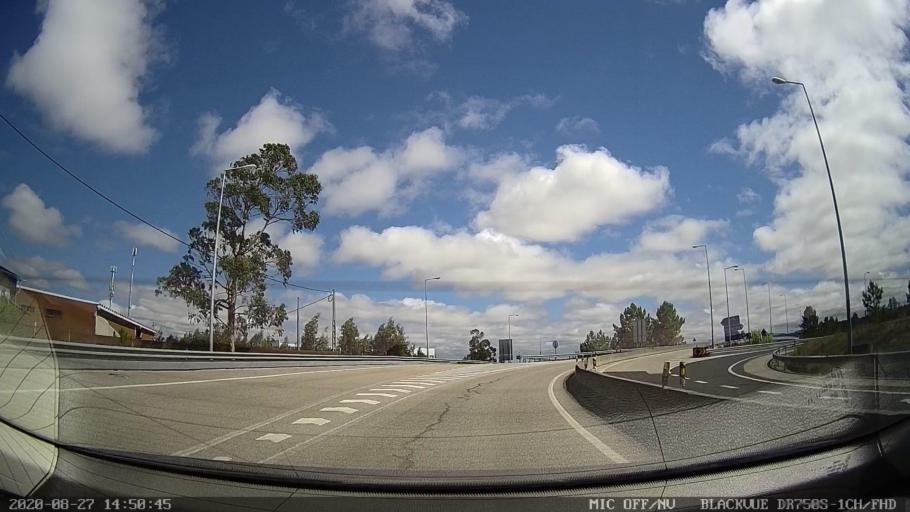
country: PT
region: Leiria
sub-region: Leiria
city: Maceira
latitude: 39.7439
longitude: -8.8731
